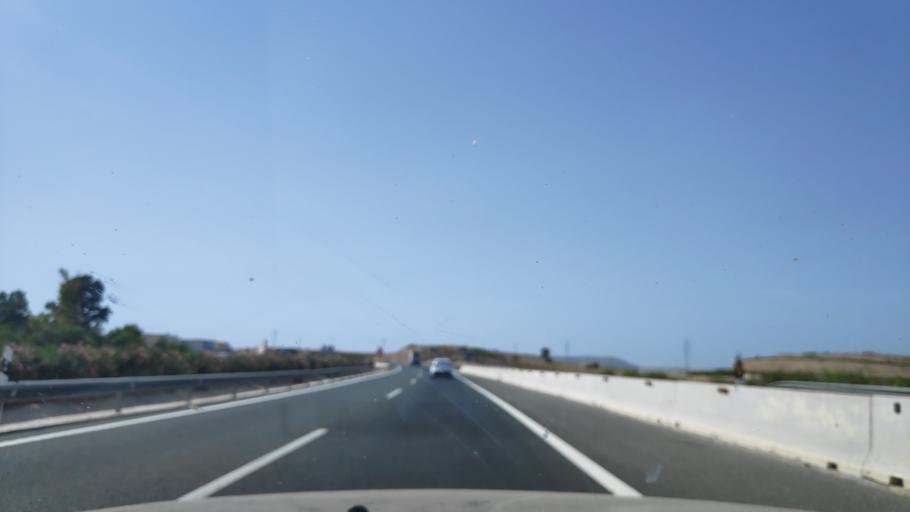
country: ES
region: Murcia
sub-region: Murcia
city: Blanca
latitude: 38.1933
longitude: -1.3316
